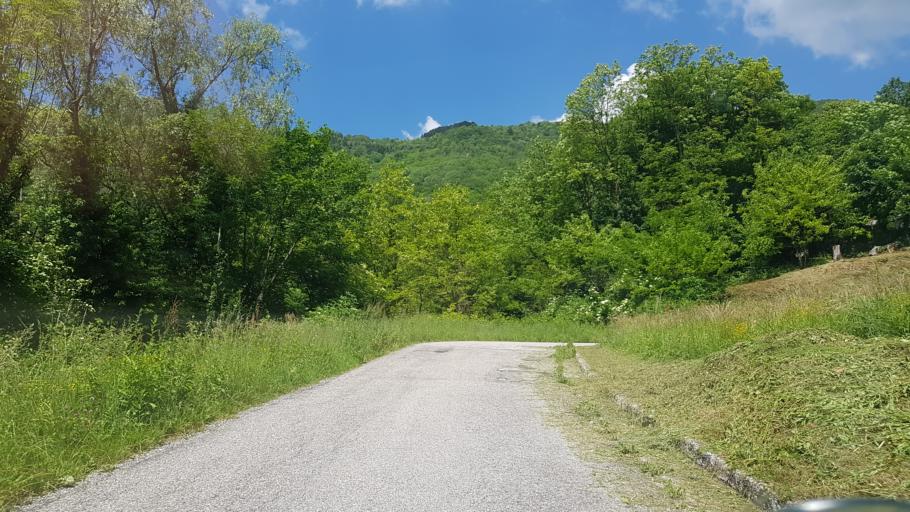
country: IT
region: Friuli Venezia Giulia
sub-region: Provincia di Udine
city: Torreano
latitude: 46.1700
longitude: 13.4275
